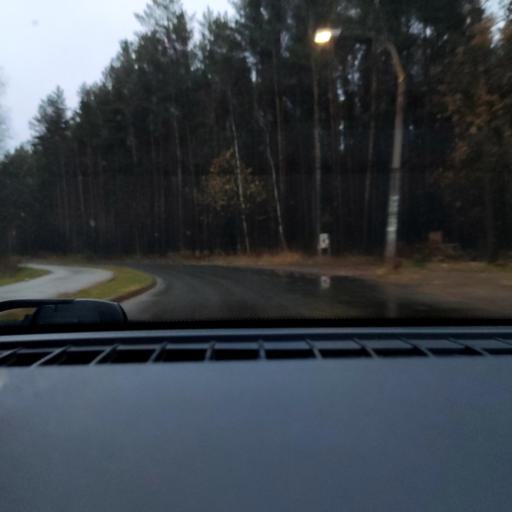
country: RU
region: Perm
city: Perm
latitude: 58.0516
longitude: 56.2247
